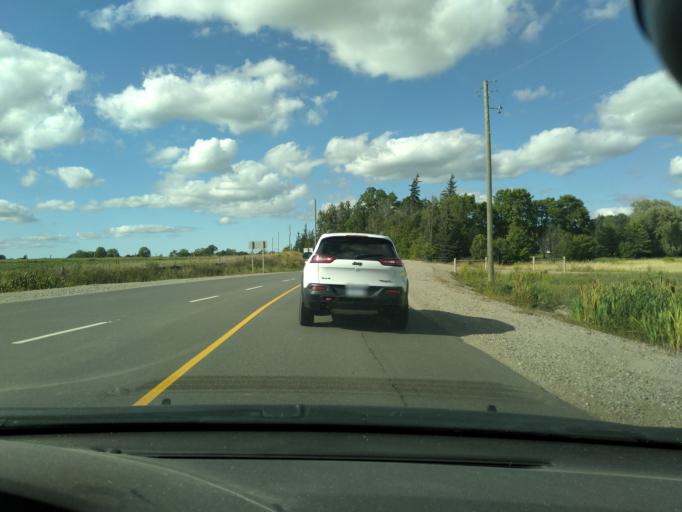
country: CA
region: Ontario
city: Bradford West Gwillimbury
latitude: 44.0738
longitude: -79.6333
